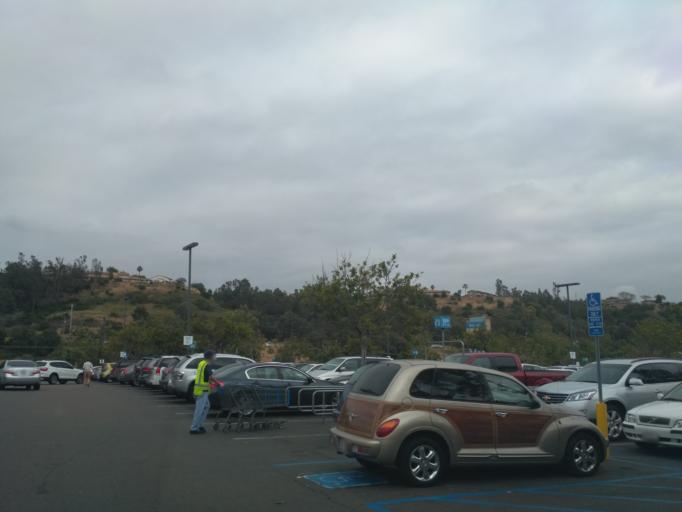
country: US
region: California
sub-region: San Diego County
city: San Diego
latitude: 32.8060
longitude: -117.1159
